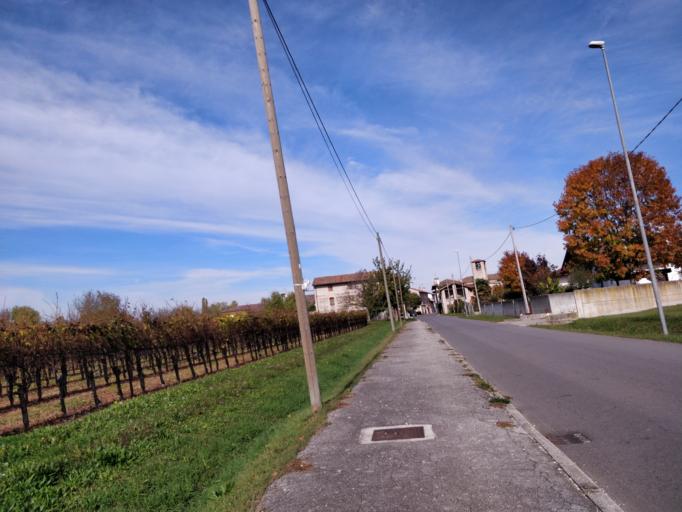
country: IT
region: Friuli Venezia Giulia
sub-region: Provincia di Udine
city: Bertiolo
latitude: 45.9414
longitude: 13.0249
